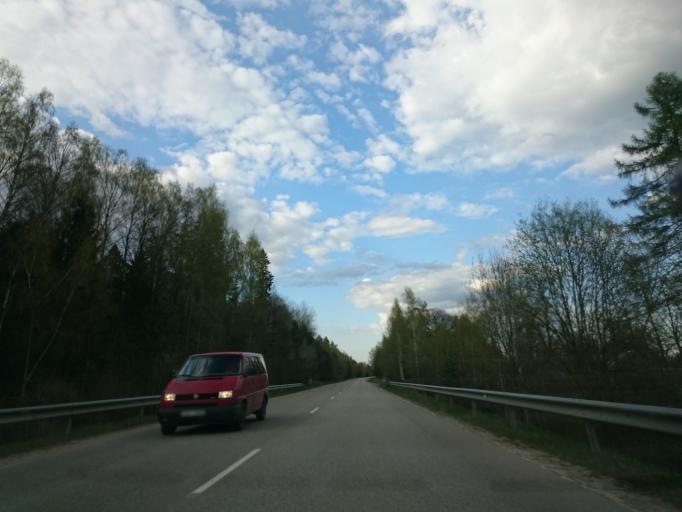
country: LV
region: Kuldigas Rajons
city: Kuldiga
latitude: 56.9463
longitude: 21.9354
